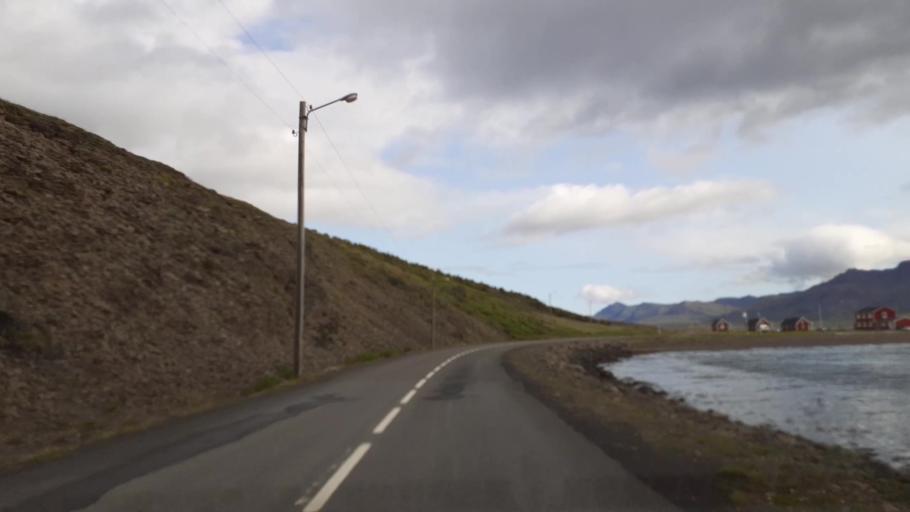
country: IS
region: East
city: Eskifjoerdur
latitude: 65.0624
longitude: -13.9939
